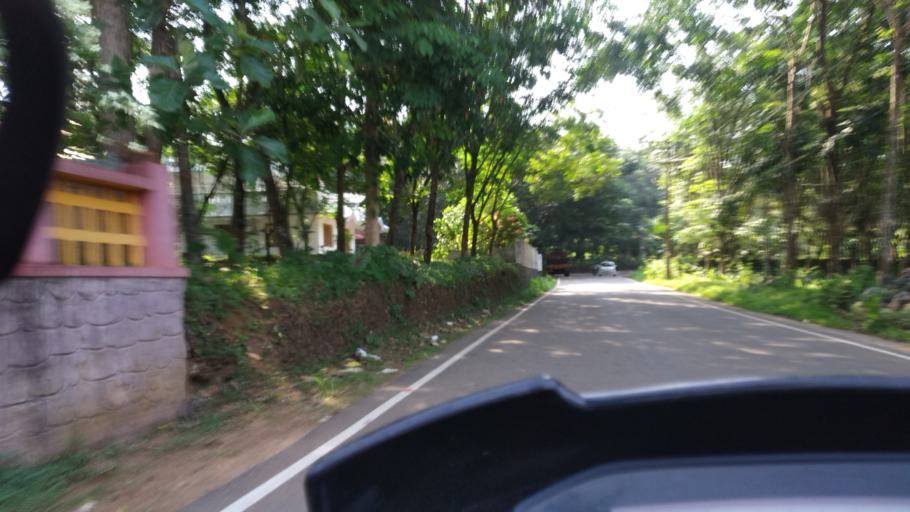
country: IN
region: Kerala
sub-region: Ernakulam
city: Piravam
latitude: 9.8573
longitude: 76.5214
